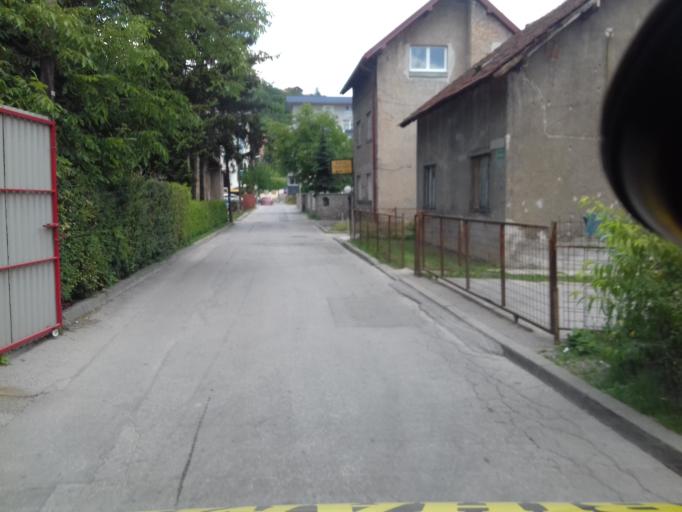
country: BA
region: Federation of Bosnia and Herzegovina
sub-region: Kanton Sarajevo
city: Sarajevo
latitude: 43.8545
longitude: 18.3782
